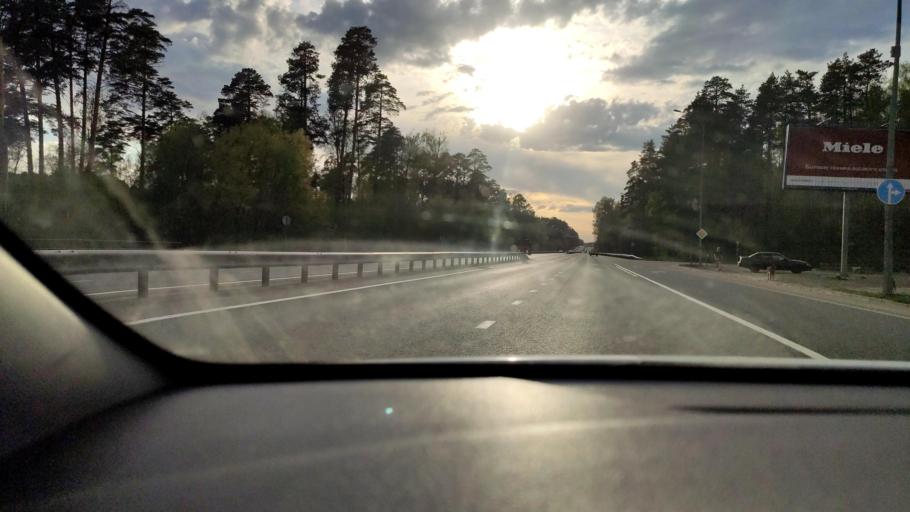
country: RU
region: Tatarstan
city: Staroye Arakchino
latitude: 55.8378
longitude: 48.9638
